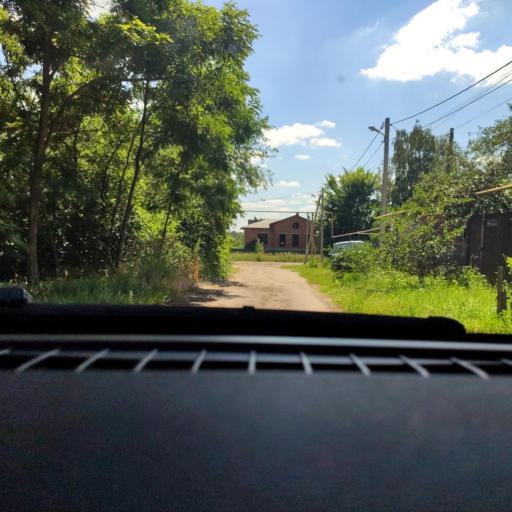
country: RU
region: Voronezj
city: Somovo
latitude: 51.6988
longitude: 39.3231
